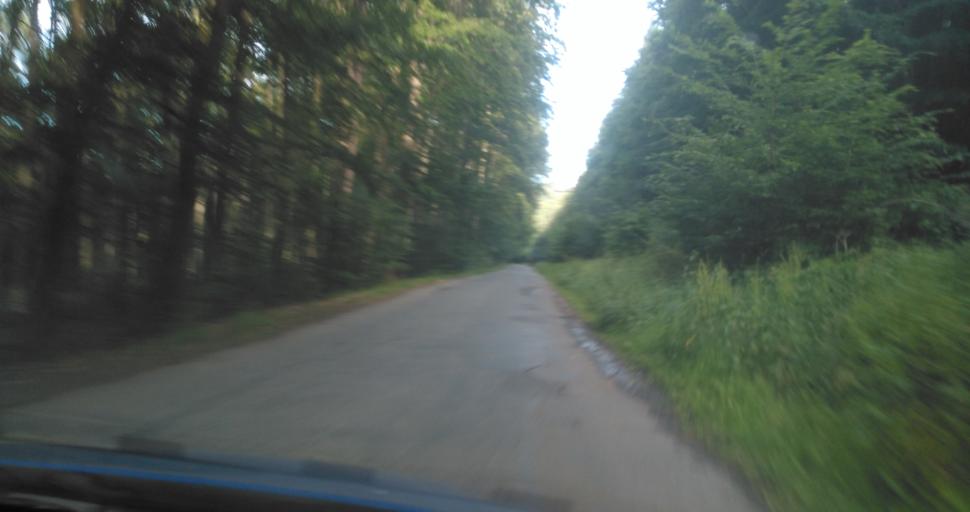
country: CZ
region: Central Bohemia
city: Roztoky
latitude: 50.0022
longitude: 13.8567
